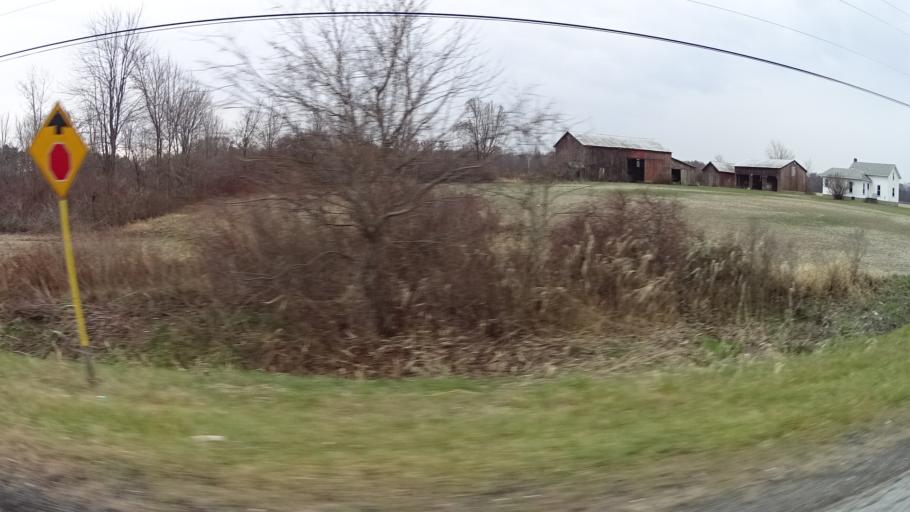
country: US
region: Ohio
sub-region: Lorain County
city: Grafton
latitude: 41.2376
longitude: -82.0258
